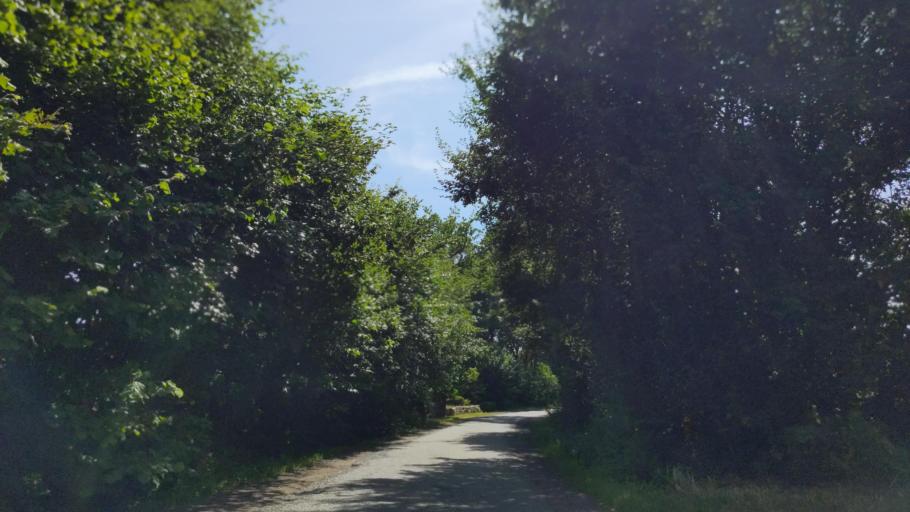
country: DE
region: Schleswig-Holstein
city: Altenkrempe
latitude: 54.1521
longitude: 10.8337
